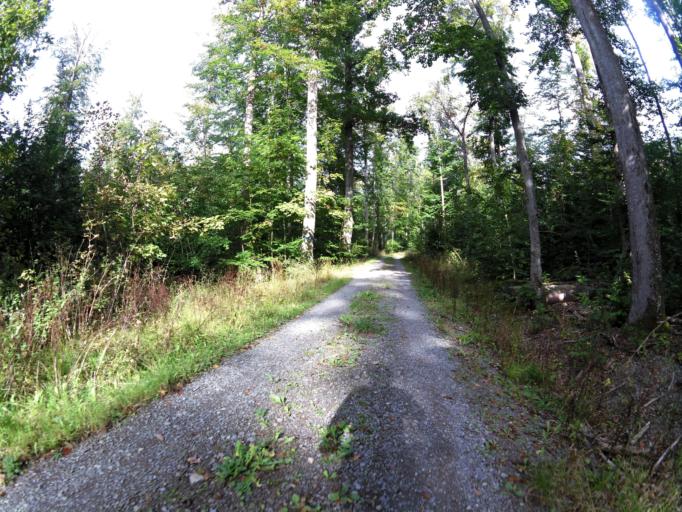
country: DE
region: Bavaria
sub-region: Regierungsbezirk Unterfranken
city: Waldbrunn
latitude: 49.7278
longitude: 9.8039
